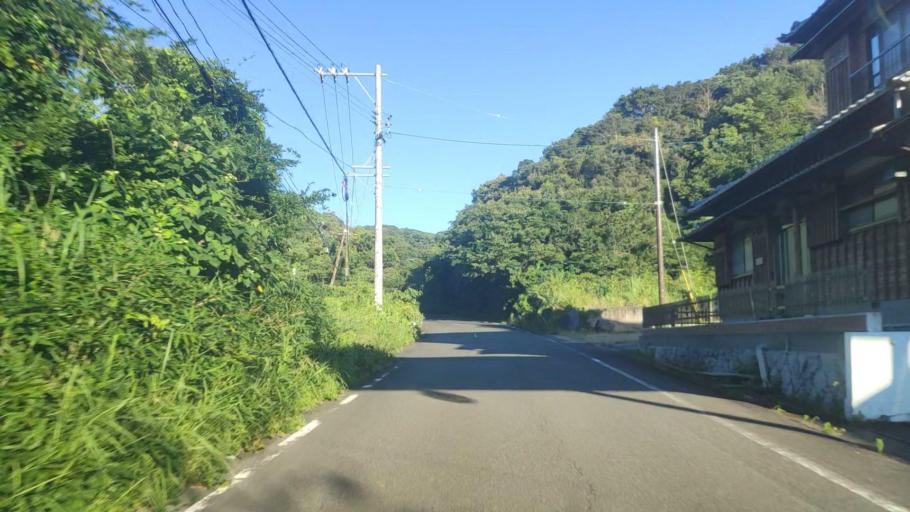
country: JP
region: Mie
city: Ise
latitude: 34.2695
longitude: 136.7673
